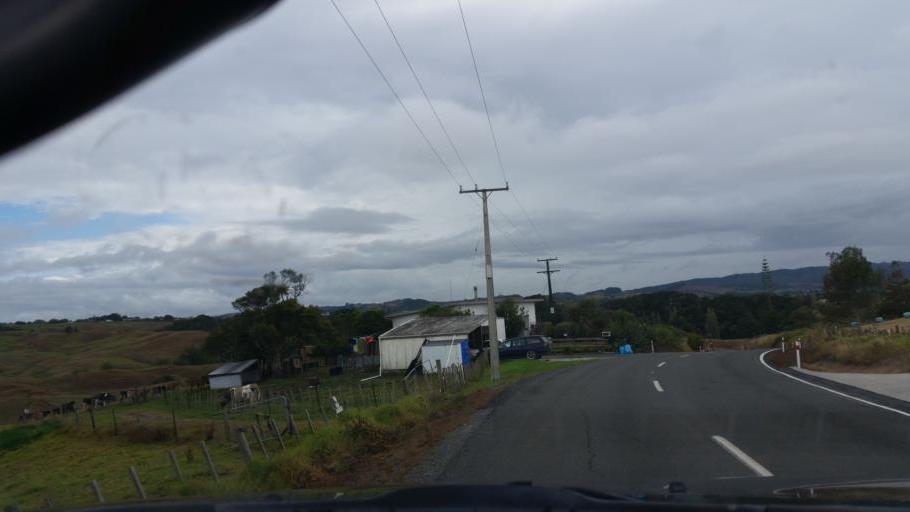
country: NZ
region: Auckland
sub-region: Auckland
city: Wellsford
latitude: -36.1267
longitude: 174.3580
